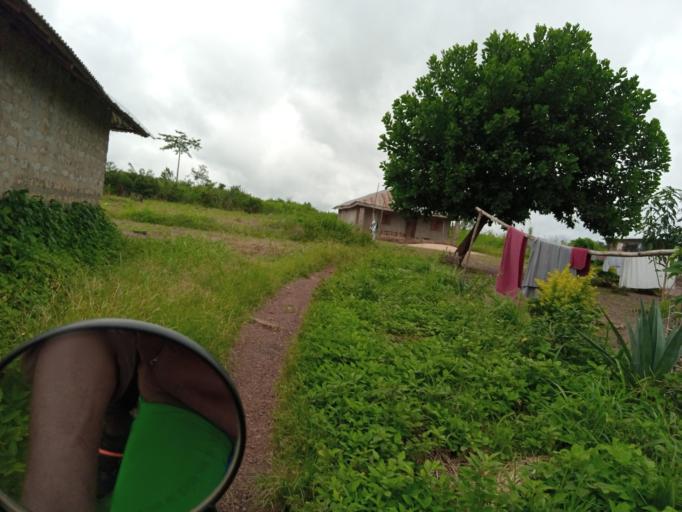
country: SL
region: Southern Province
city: Largo
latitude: 8.1935
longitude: -12.0548
